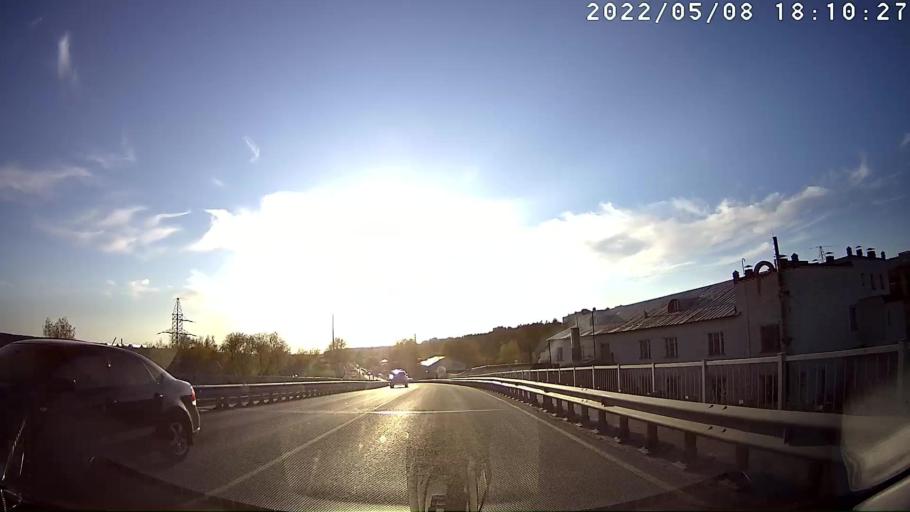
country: RU
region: Tatarstan
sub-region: Zelenodol'skiy Rayon
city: Zelenodolsk
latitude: 55.8391
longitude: 48.5245
